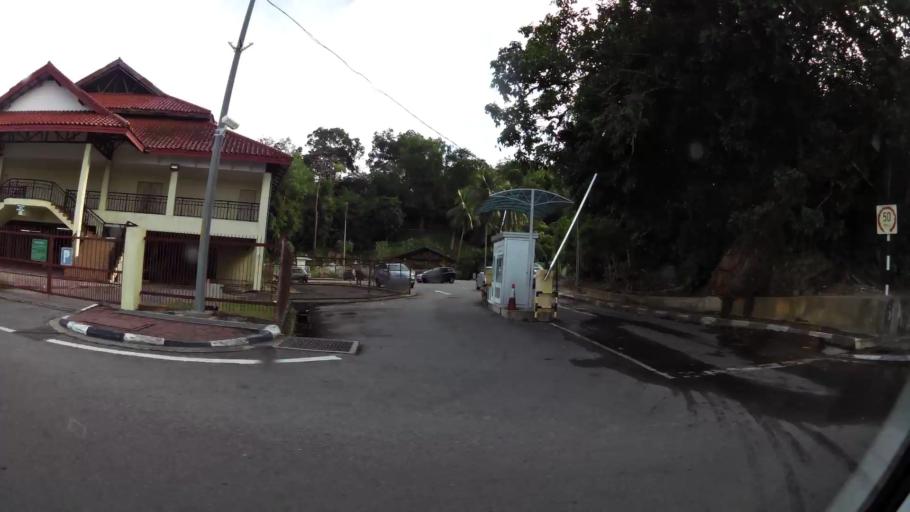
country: BN
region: Brunei and Muara
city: Bandar Seri Begawan
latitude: 4.8872
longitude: 114.9453
